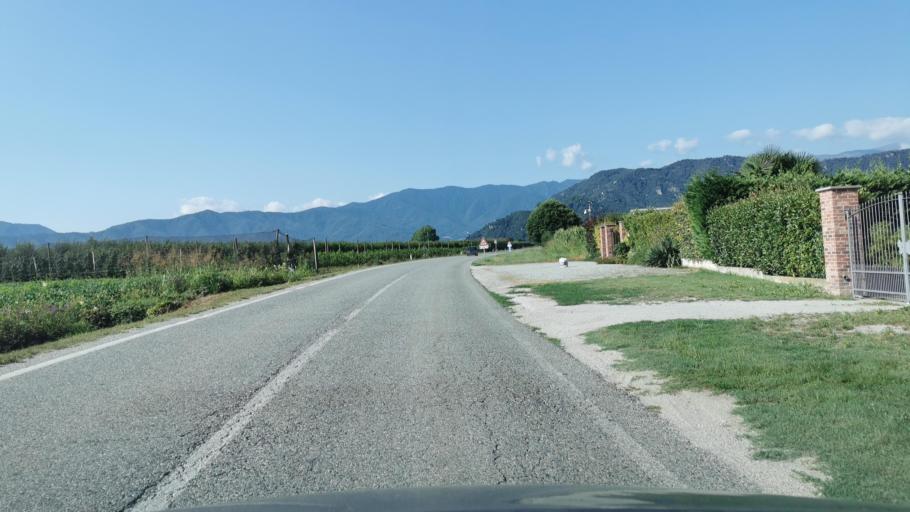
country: IT
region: Piedmont
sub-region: Provincia di Cuneo
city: Revello
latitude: 44.6792
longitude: 7.4107
